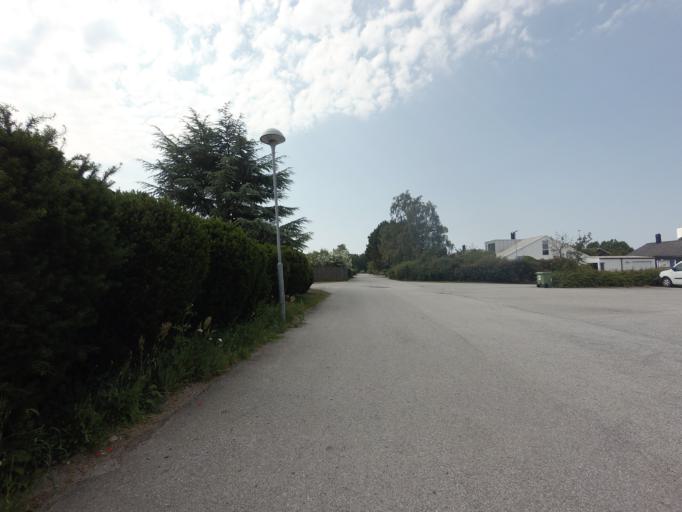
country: SE
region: Skane
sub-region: Vellinge Kommun
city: Skanor med Falsterbo
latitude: 55.4047
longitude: 12.8516
